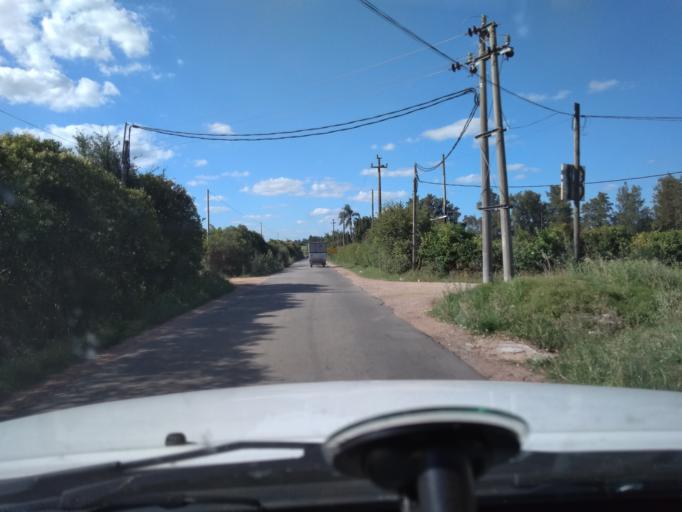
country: UY
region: Canelones
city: La Paz
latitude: -34.7948
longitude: -56.2114
